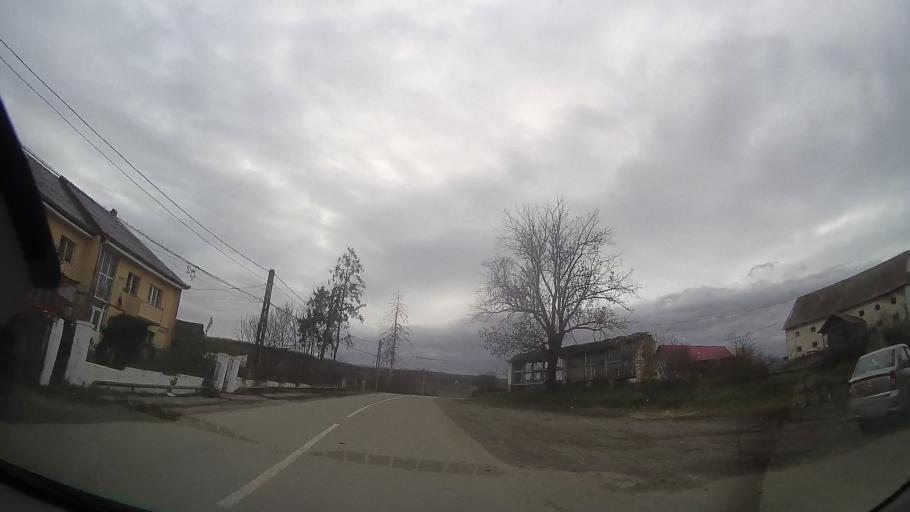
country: RO
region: Bistrita-Nasaud
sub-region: Comuna Milas
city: Milas
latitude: 46.8172
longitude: 24.4380
